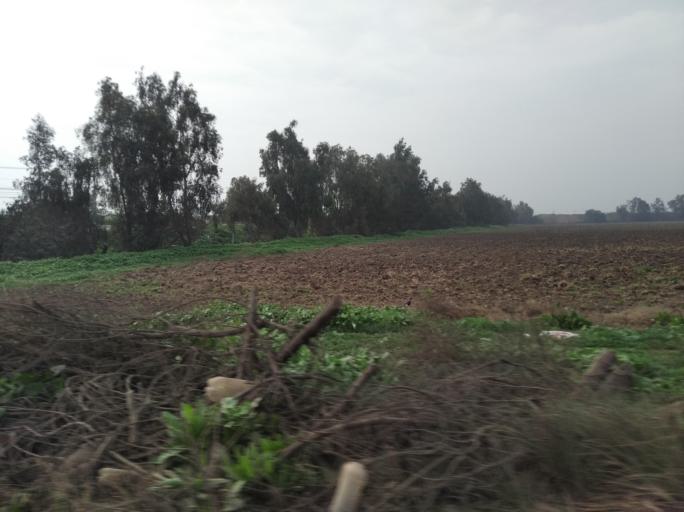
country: CL
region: Santiago Metropolitan
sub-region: Provincia de Chacabuco
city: Lampa
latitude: -33.3522
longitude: -70.8017
